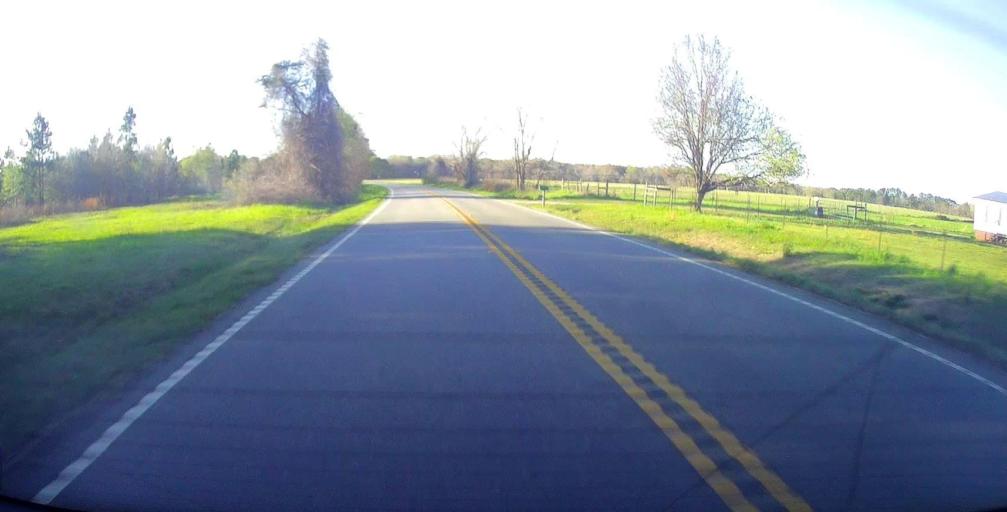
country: US
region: Georgia
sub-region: Pulaski County
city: Hawkinsville
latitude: 32.1867
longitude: -83.3656
